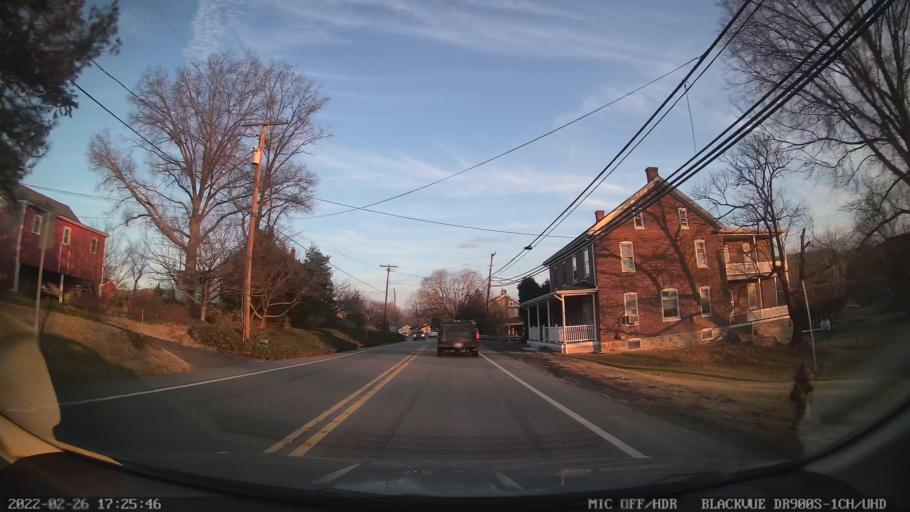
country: US
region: Pennsylvania
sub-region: Montgomery County
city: East Greenville
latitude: 40.4269
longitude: -75.5328
